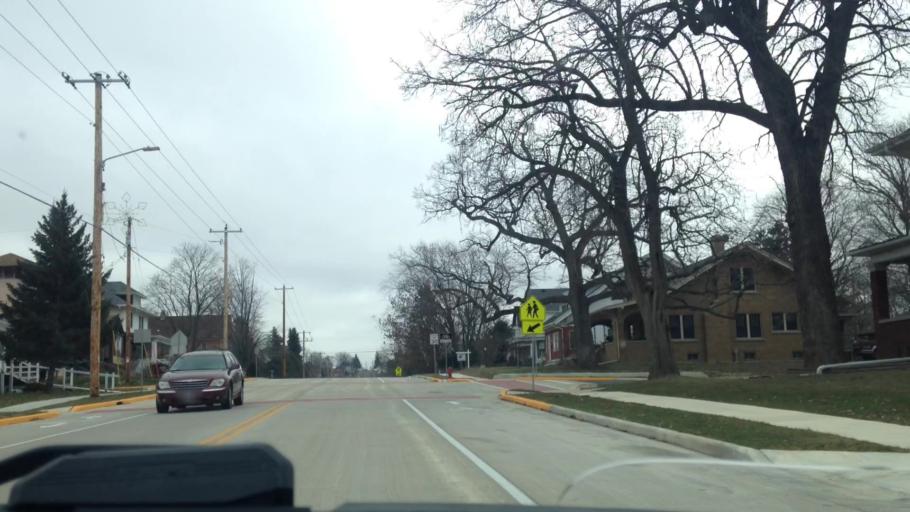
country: US
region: Wisconsin
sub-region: Dodge County
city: Mayville
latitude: 43.4939
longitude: -88.5504
